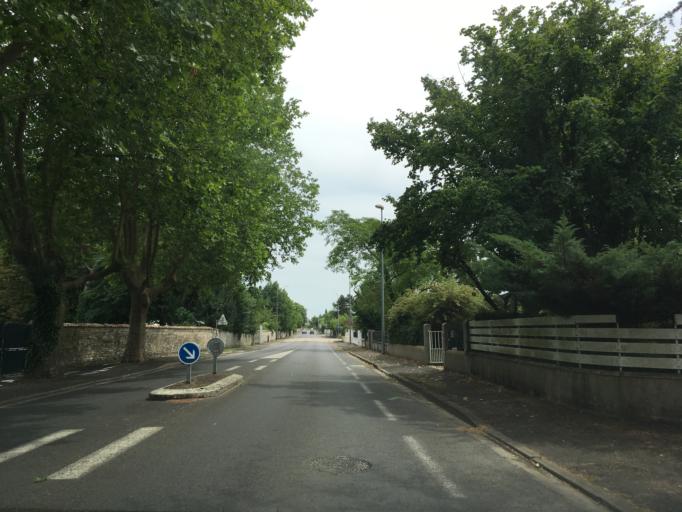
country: FR
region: Poitou-Charentes
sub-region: Departement des Deux-Sevres
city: Bessines
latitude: 46.3224
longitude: -0.5117
